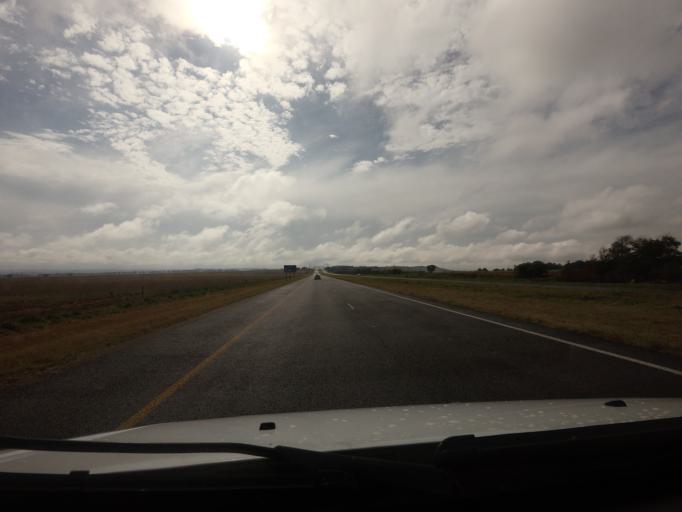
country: ZA
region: Gauteng
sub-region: City of Tshwane Metropolitan Municipality
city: Cullinan
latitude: -25.7976
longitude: 28.5343
